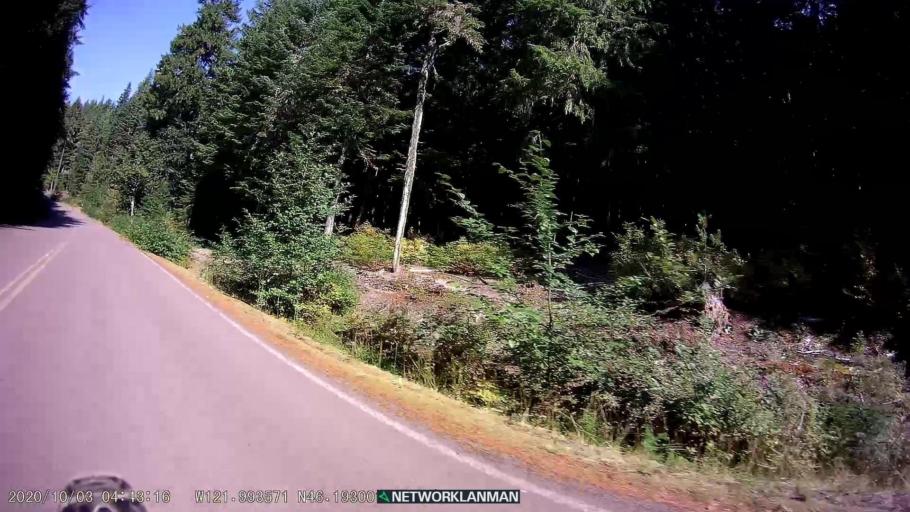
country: US
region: Washington
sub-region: Lewis County
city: Morton
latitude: 46.1933
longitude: -121.9934
